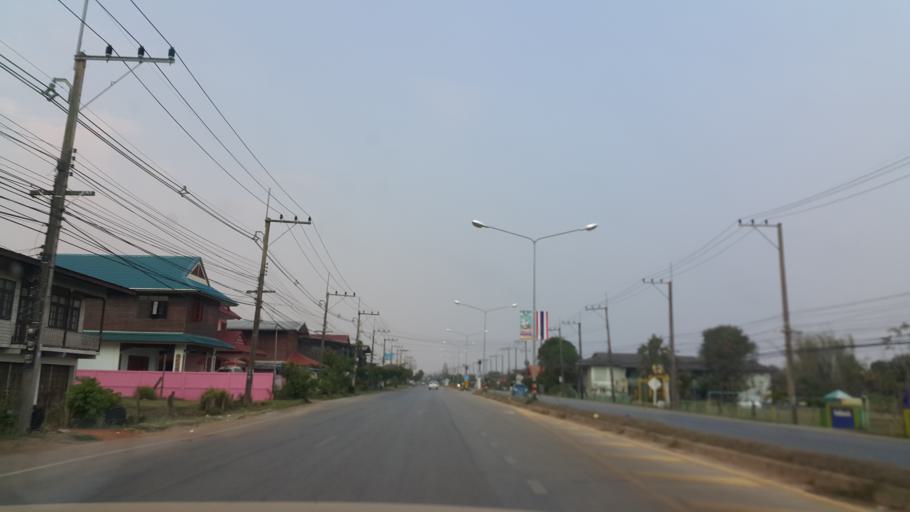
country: TH
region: Nakhon Phanom
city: That Phanom
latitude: 16.9740
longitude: 104.7273
